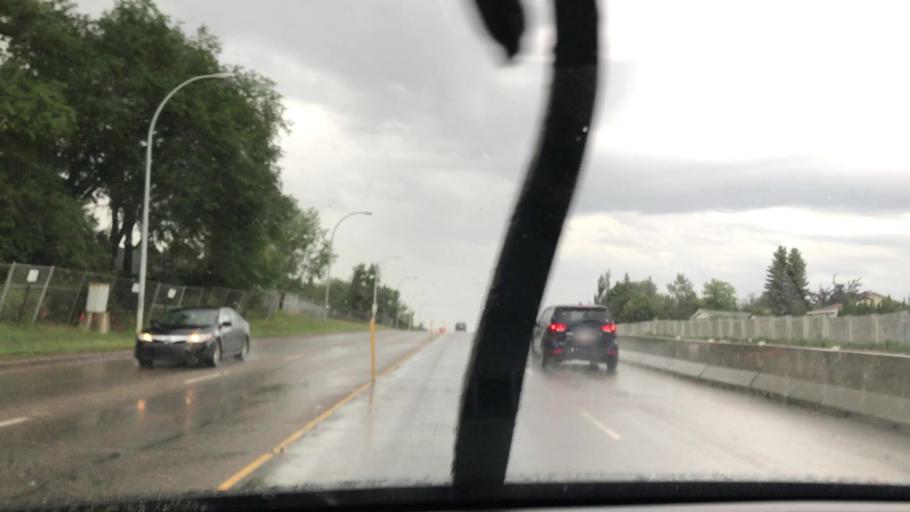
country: CA
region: Alberta
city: Edmonton
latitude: 53.4673
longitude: -113.4370
